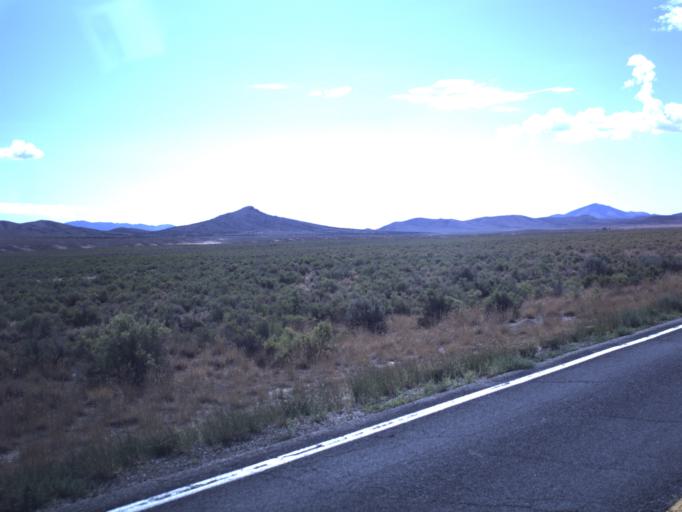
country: US
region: Utah
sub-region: Tooele County
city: Tooele
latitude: 40.1386
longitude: -112.4308
